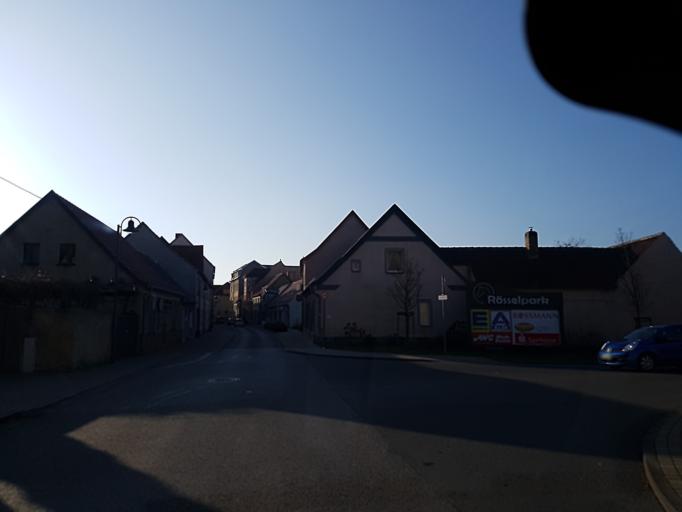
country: DE
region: Brandenburg
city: Bad Liebenwerda
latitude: 51.5180
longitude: 13.3952
